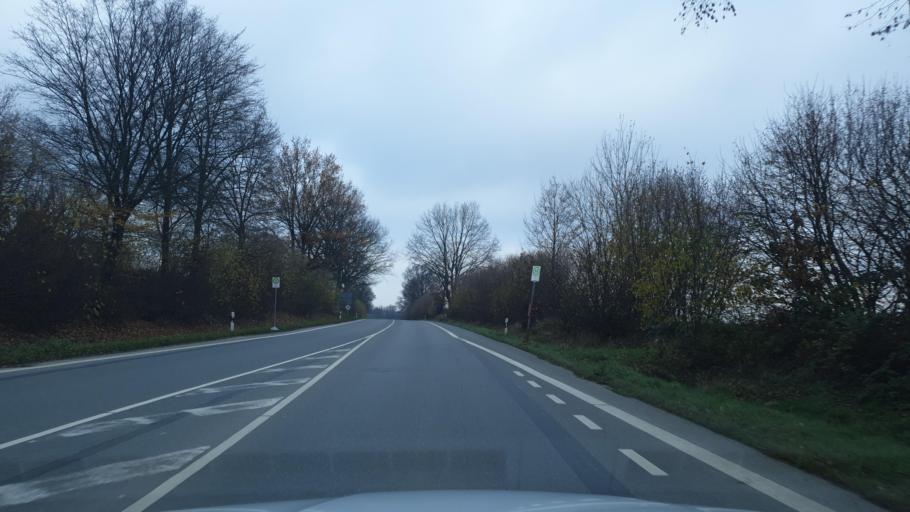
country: DE
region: North Rhine-Westphalia
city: Enger
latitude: 52.0922
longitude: 8.5860
